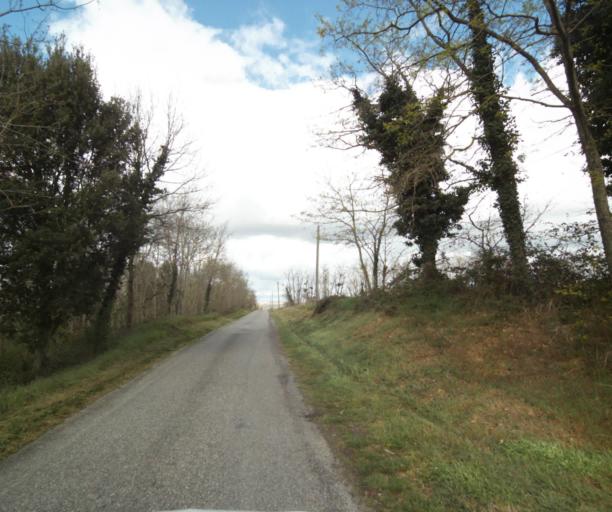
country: FR
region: Midi-Pyrenees
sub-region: Departement de l'Ariege
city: Saverdun
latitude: 43.2678
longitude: 1.5826
